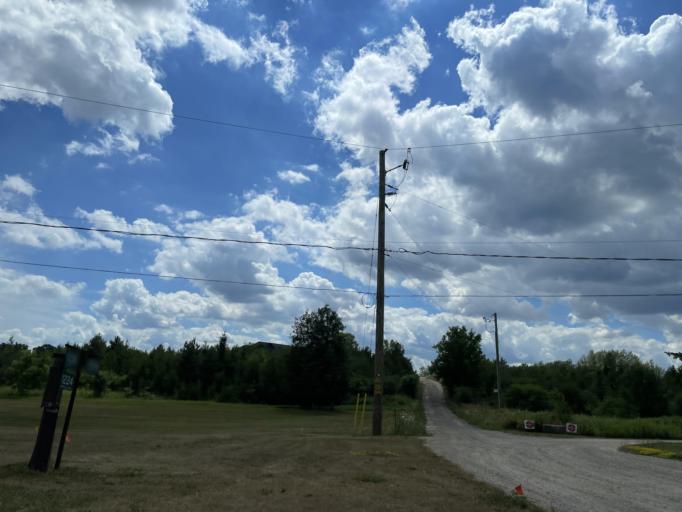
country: CA
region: Ontario
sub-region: Wellington County
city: Guelph
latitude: 43.5317
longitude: -80.3877
